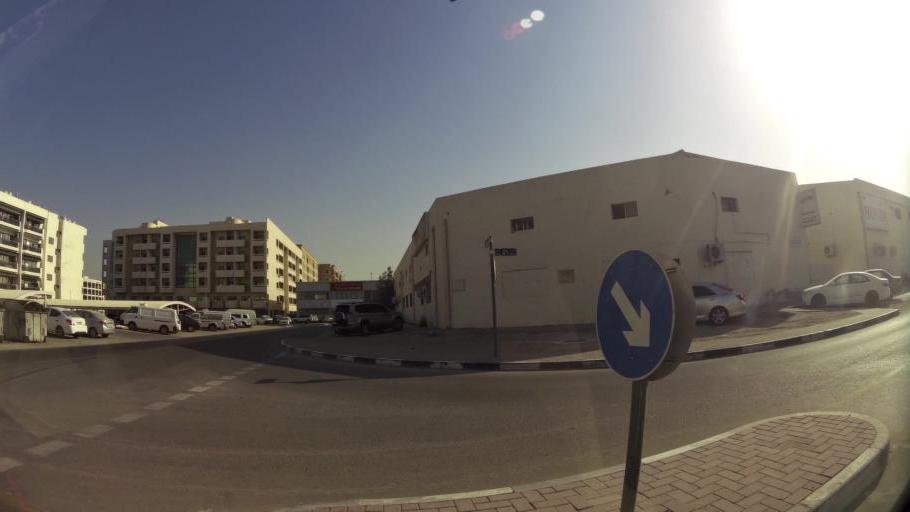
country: AE
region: Ash Shariqah
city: Sharjah
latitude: 25.2897
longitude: 55.3917
